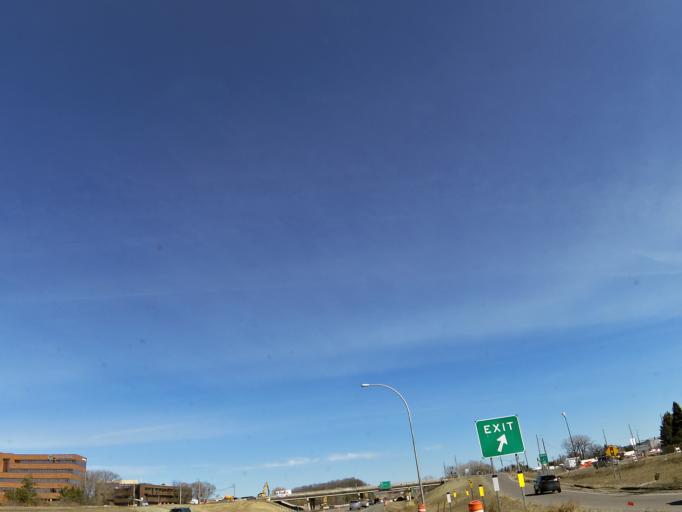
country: US
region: Minnesota
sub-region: Hennepin County
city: Eden Prairie
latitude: 44.8797
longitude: -93.4138
